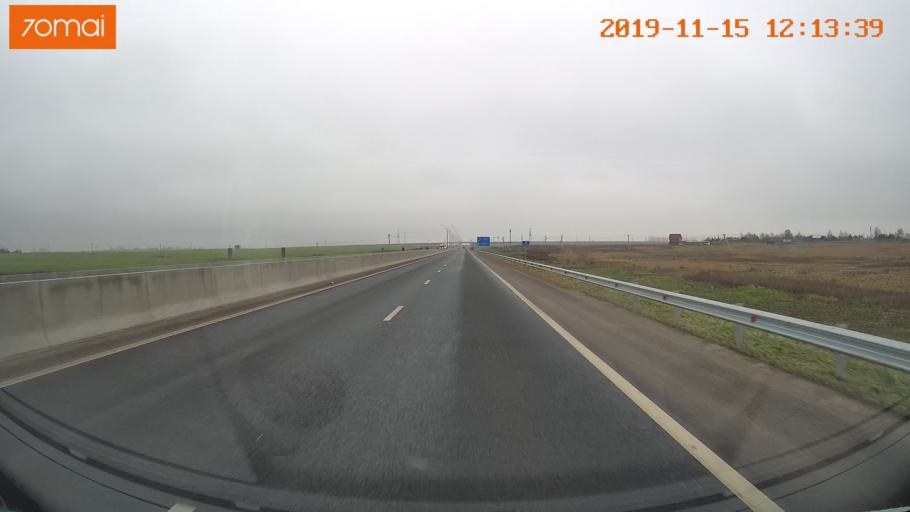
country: RU
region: Vologda
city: Vologda
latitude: 59.1634
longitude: 39.7925
